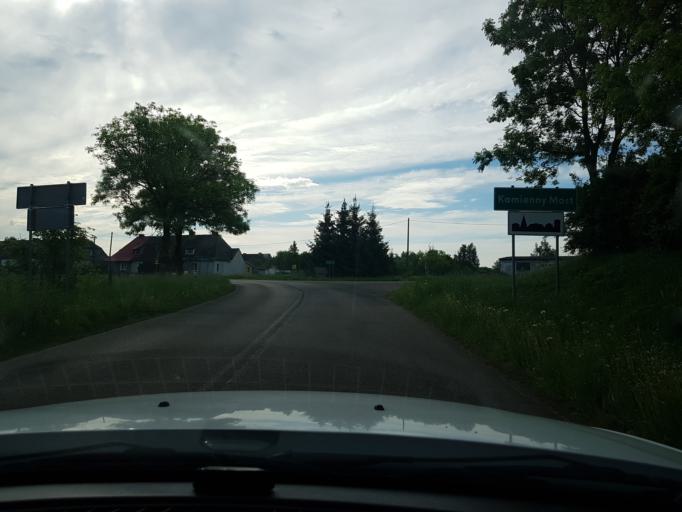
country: PL
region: West Pomeranian Voivodeship
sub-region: Powiat stargardzki
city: Chociwel
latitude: 53.4572
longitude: 15.3806
